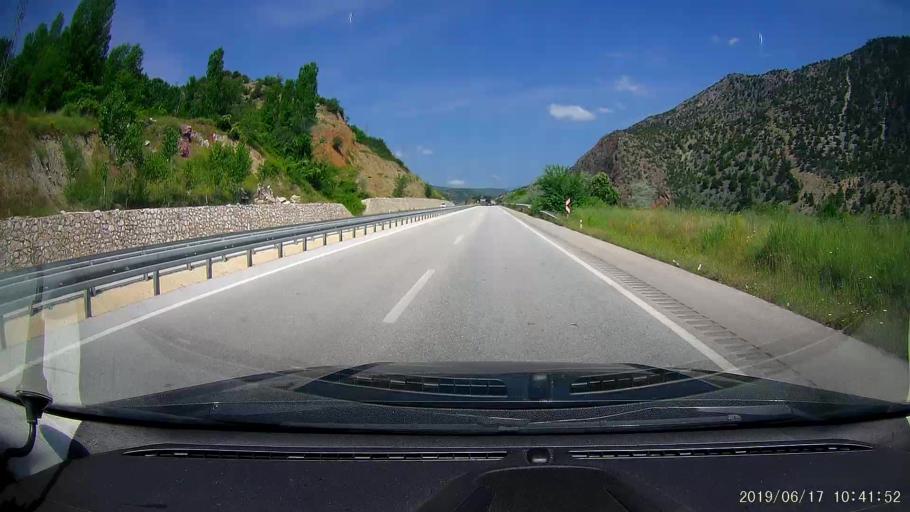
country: TR
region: Corum
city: Kargi
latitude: 41.0439
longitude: 34.5663
